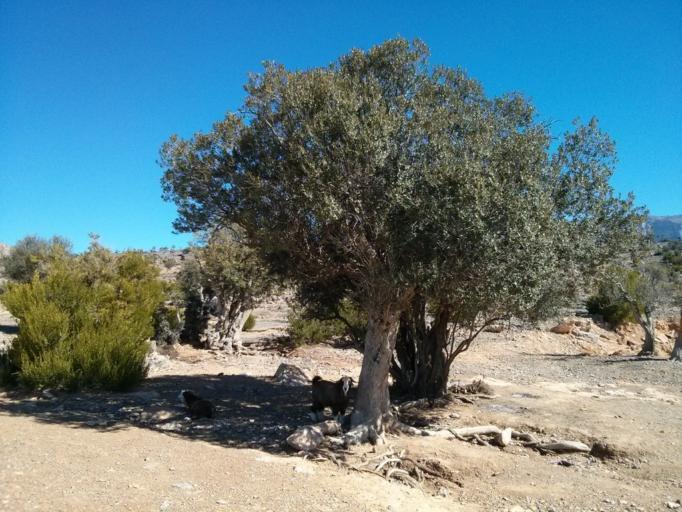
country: OM
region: Muhafazat ad Dakhiliyah
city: Bahla'
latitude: 23.2075
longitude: 57.1984
